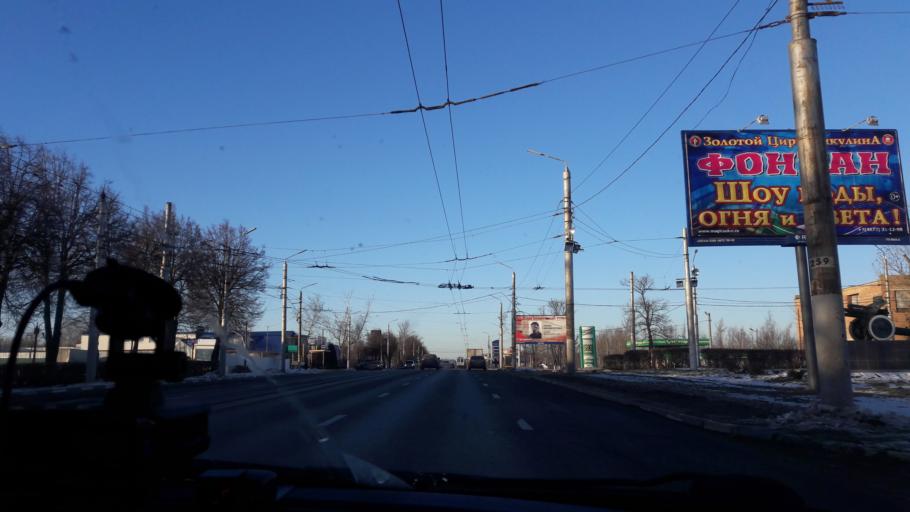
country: RU
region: Tula
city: Gorelki
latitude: 54.2391
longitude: 37.6202
